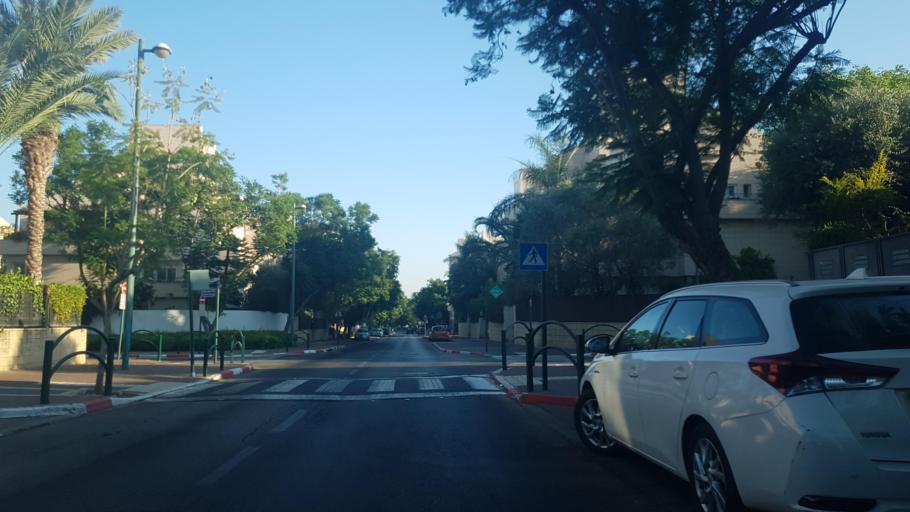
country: IL
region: Central District
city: Kfar Saba
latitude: 32.1806
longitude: 34.9352
